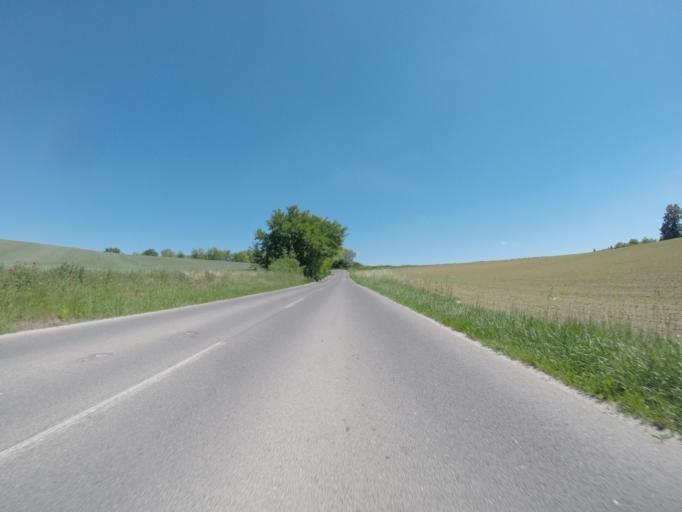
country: SK
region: Trnavsky
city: Hlohovec
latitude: 48.4605
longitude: 17.8482
